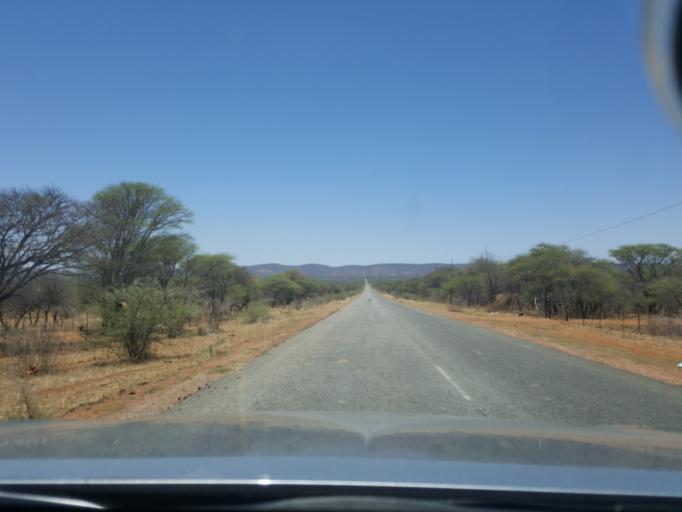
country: BW
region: South East
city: Lobatse
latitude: -25.2184
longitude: 25.9421
